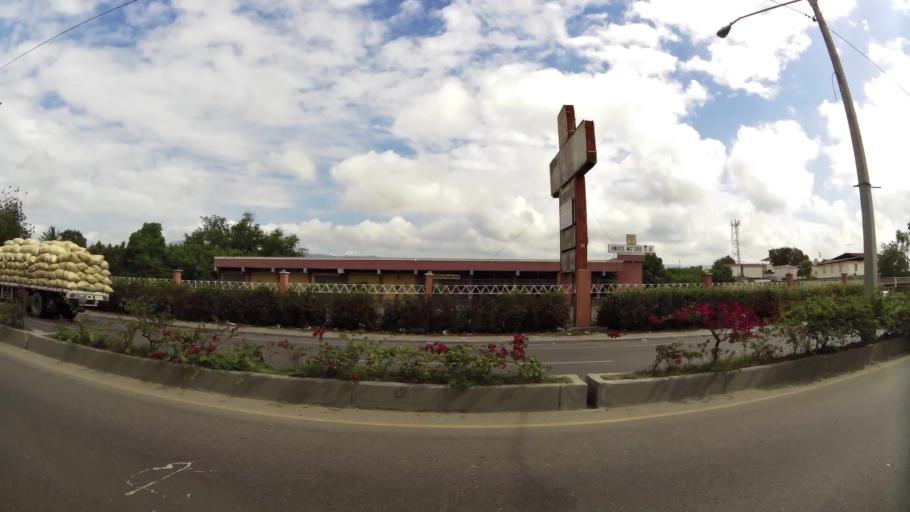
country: DO
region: Santiago
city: Santiago de los Caballeros
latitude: 19.4903
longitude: -70.7235
